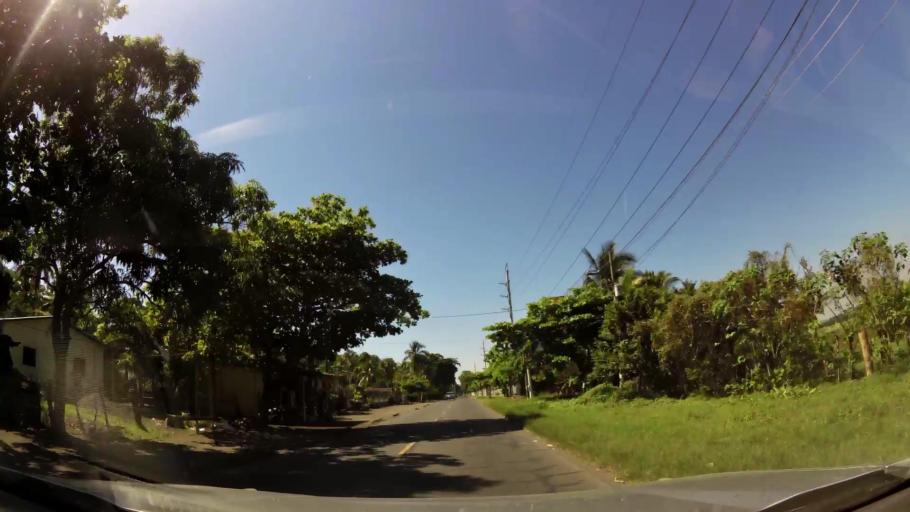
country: GT
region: Escuintla
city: Iztapa
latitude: 13.9373
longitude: -90.7281
